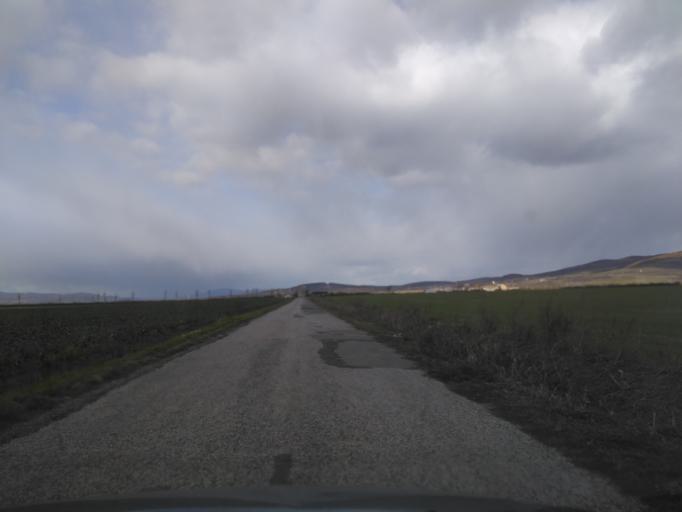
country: HU
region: Borsod-Abauj-Zemplen
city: Satoraljaujhely
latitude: 48.4143
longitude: 21.6794
